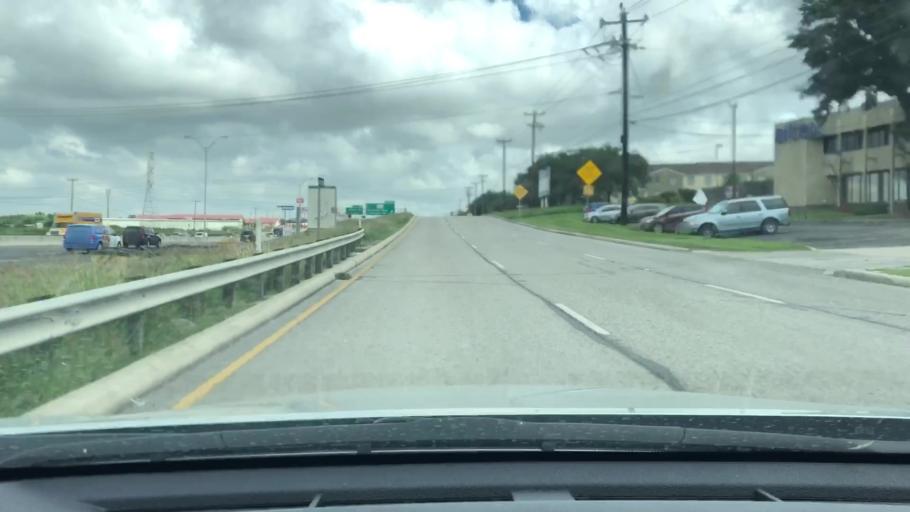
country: US
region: Texas
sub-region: Bexar County
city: Windcrest
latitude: 29.5425
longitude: -98.3740
